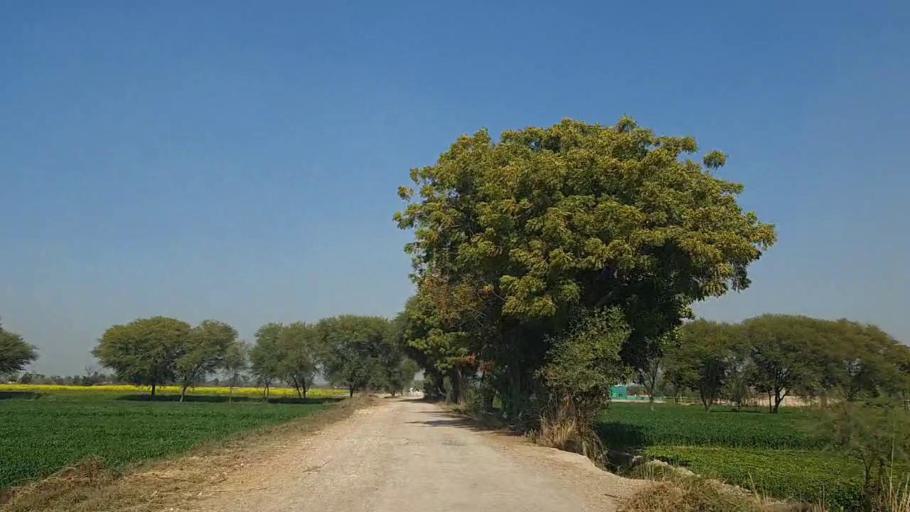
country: PK
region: Sindh
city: Nawabshah
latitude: 26.2314
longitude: 68.3380
